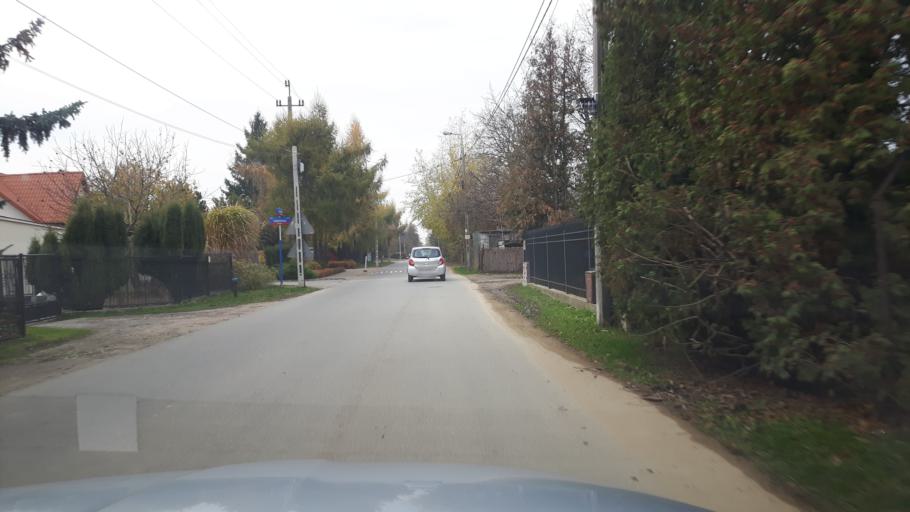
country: PL
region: Masovian Voivodeship
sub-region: Warszawa
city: Wilanow
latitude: 52.1647
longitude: 21.1195
